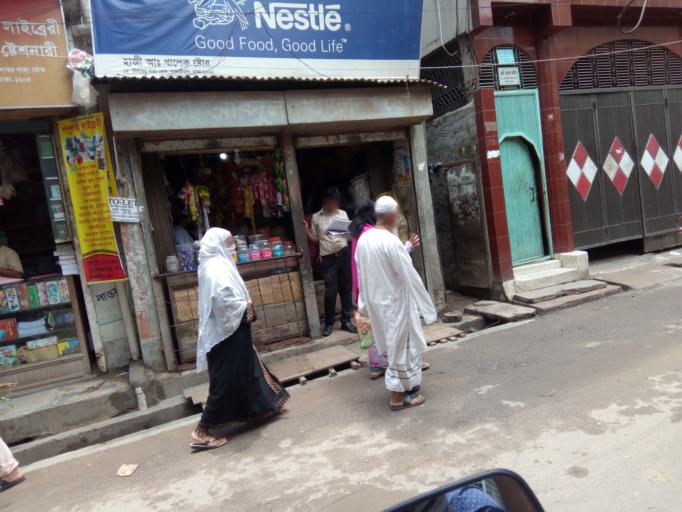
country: BD
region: Dhaka
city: Azimpur
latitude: 23.7256
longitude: 90.3742
